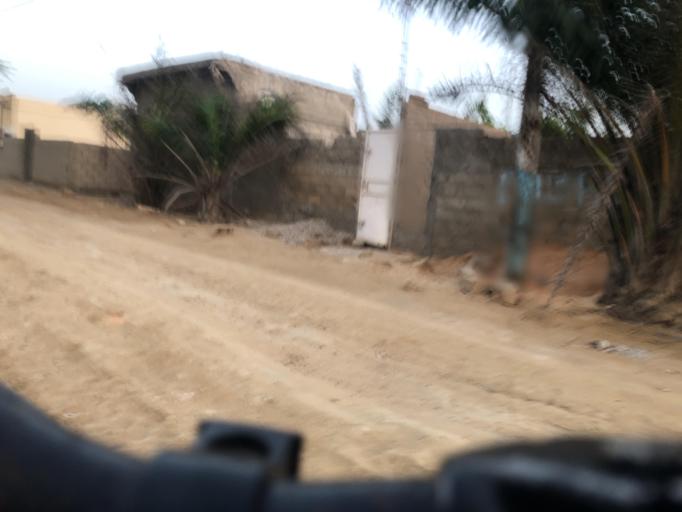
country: SN
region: Saint-Louis
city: Saint-Louis
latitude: 16.0695
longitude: -16.4314
